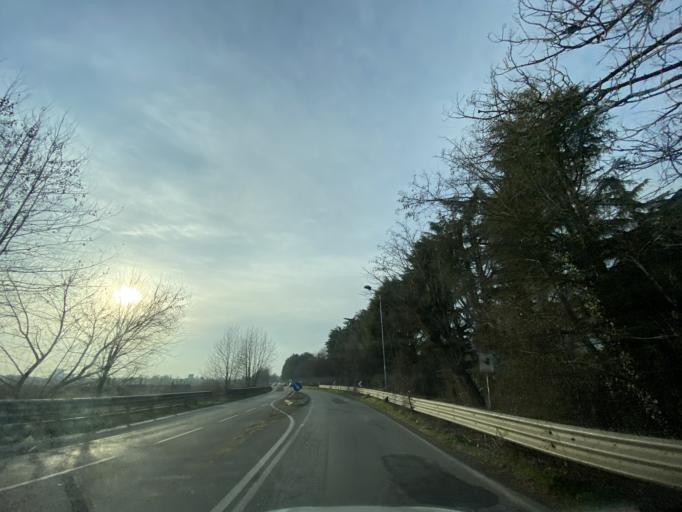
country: IT
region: Lombardy
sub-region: Citta metropolitana di Milano
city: Pioltello
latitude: 45.5138
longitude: 9.3111
